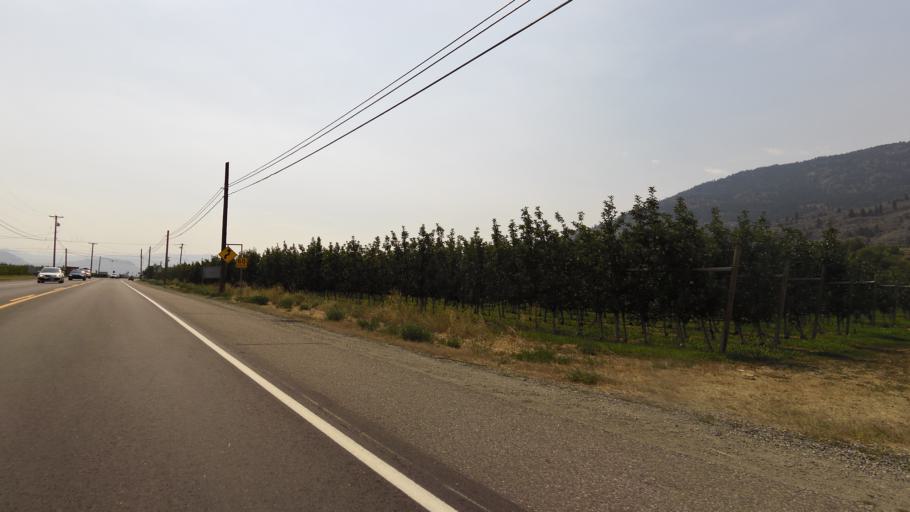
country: CA
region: British Columbia
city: Osoyoos
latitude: 49.0512
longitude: -119.5001
